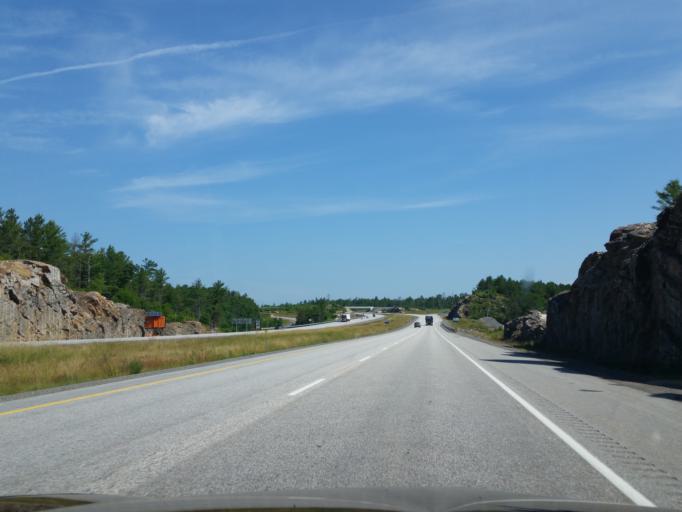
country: CA
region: Ontario
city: Greater Sudbury
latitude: 46.2187
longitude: -80.7699
